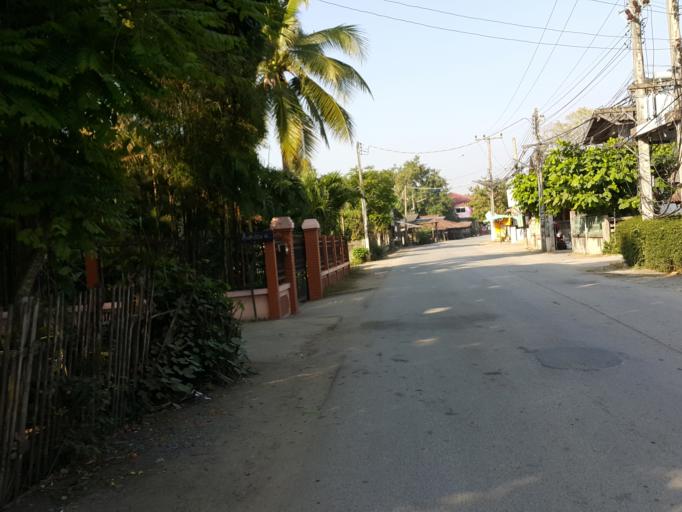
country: TH
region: Chiang Mai
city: San Kamphaeng
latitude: 18.7201
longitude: 99.1110
